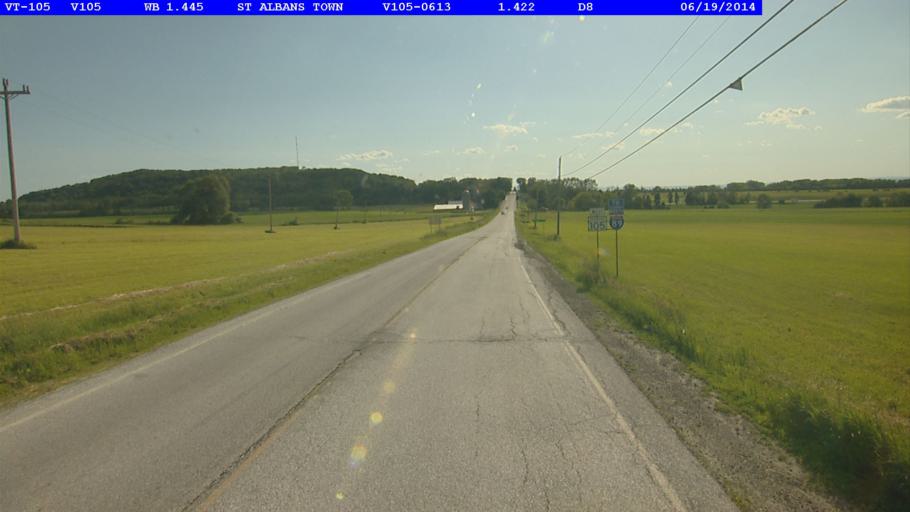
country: US
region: Vermont
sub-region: Franklin County
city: Saint Albans
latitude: 44.8291
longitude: -73.0539
